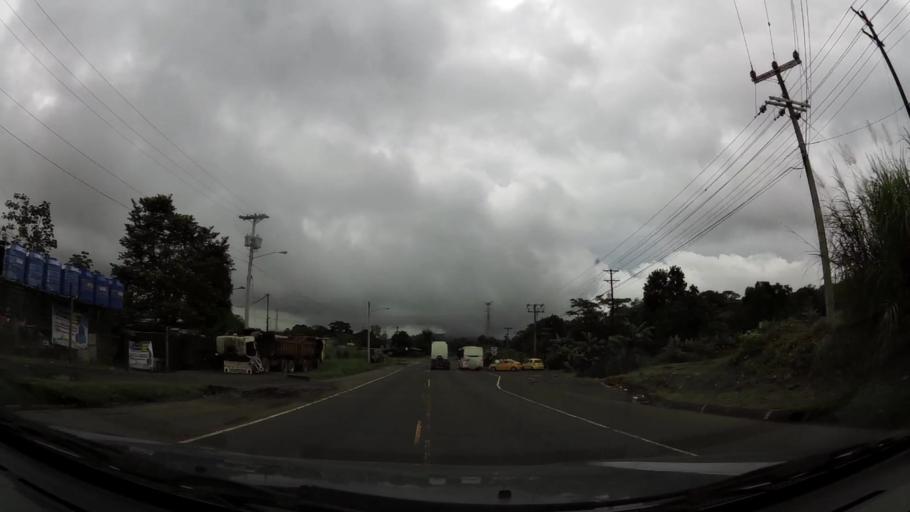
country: PA
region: Colon
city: Nuevo Vigia
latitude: 9.2009
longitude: -79.6254
